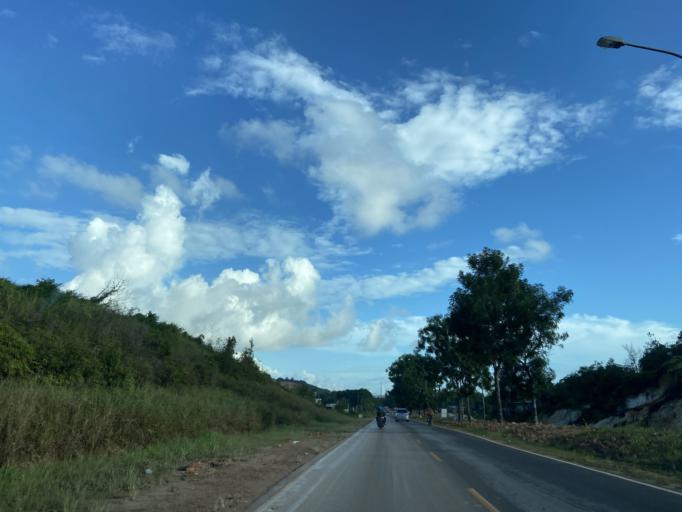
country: SG
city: Singapore
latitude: 1.0212
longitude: 104.0129
